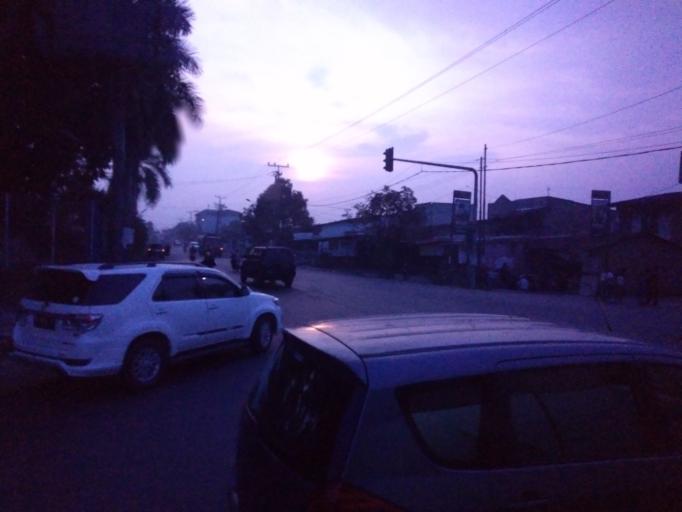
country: ID
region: North Sumatra
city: Medan
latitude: 3.6424
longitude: 98.6813
